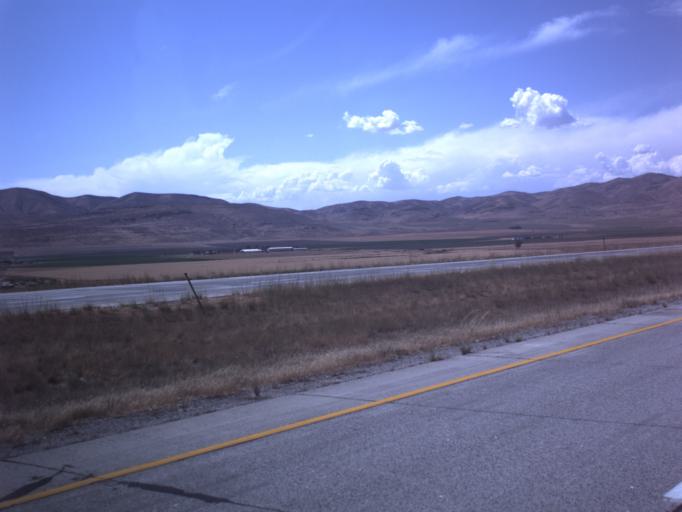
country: US
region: Utah
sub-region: Box Elder County
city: Tremonton
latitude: 41.7320
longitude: -112.2482
